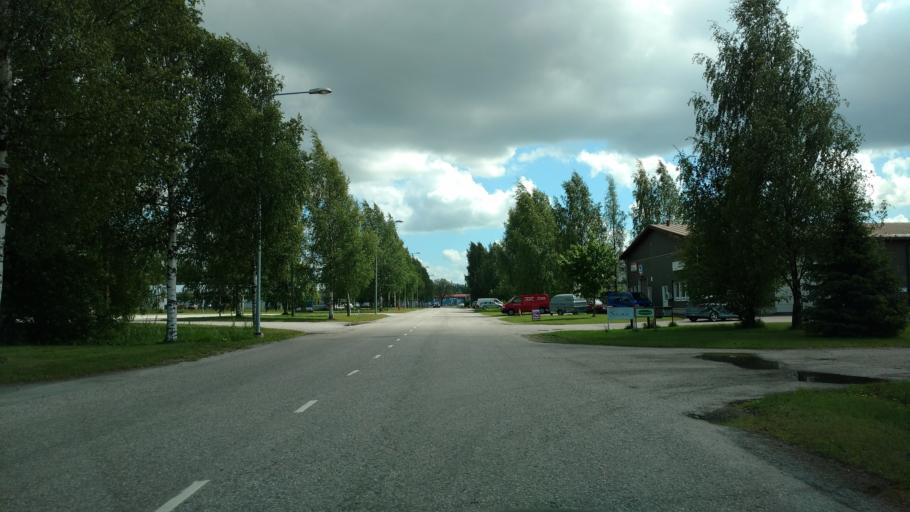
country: FI
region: Varsinais-Suomi
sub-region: Salo
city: Salo
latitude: 60.3799
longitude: 23.1083
